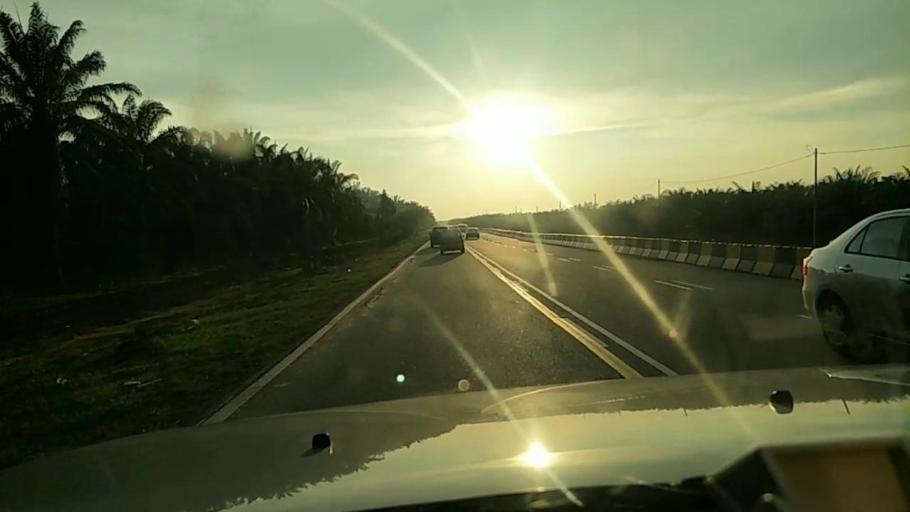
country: MY
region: Perak
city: Kampong Dungun
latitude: 3.3072
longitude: 101.3387
